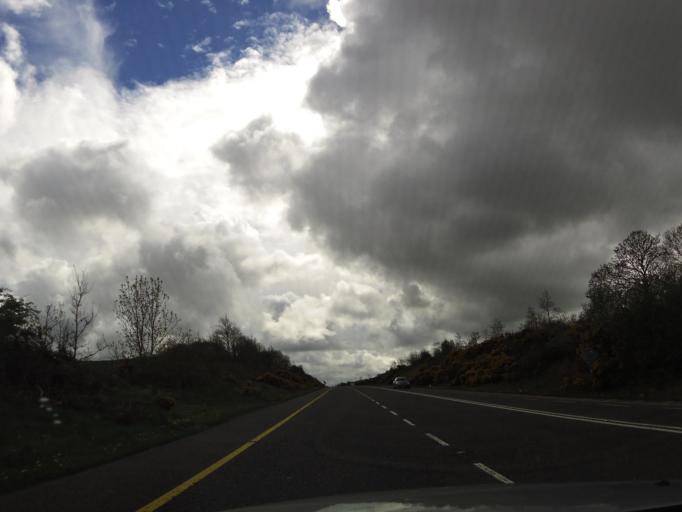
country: IE
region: Connaught
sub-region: Maigh Eo
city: Claremorris
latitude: 53.7656
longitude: -8.9594
